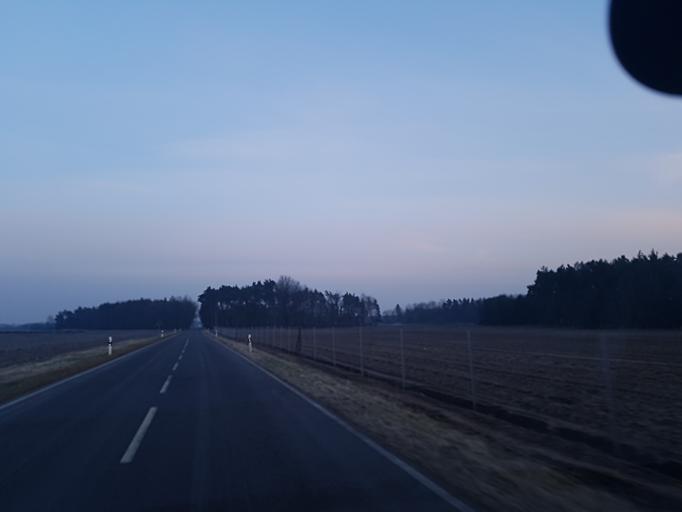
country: DE
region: Saxony-Anhalt
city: Holzdorf
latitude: 51.7597
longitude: 13.1135
